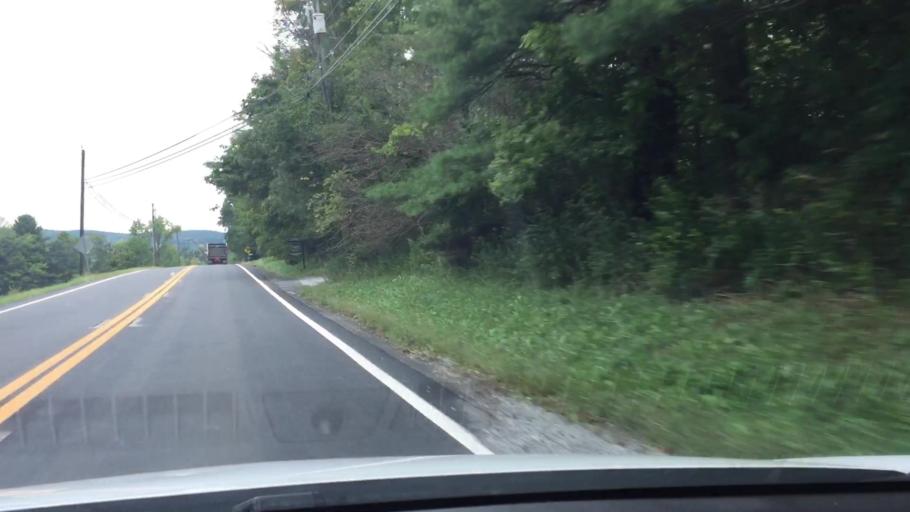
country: US
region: Massachusetts
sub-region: Berkshire County
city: Richmond
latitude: 42.3702
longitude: -73.3680
